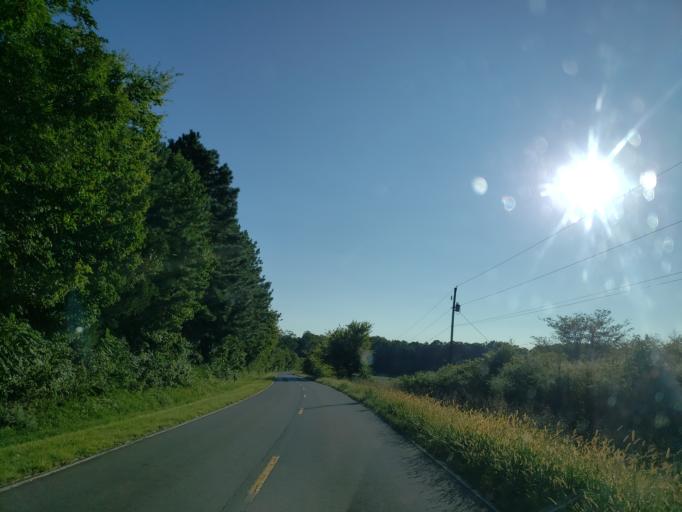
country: US
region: Georgia
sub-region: Bartow County
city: Rydal
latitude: 34.2905
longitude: -84.7933
